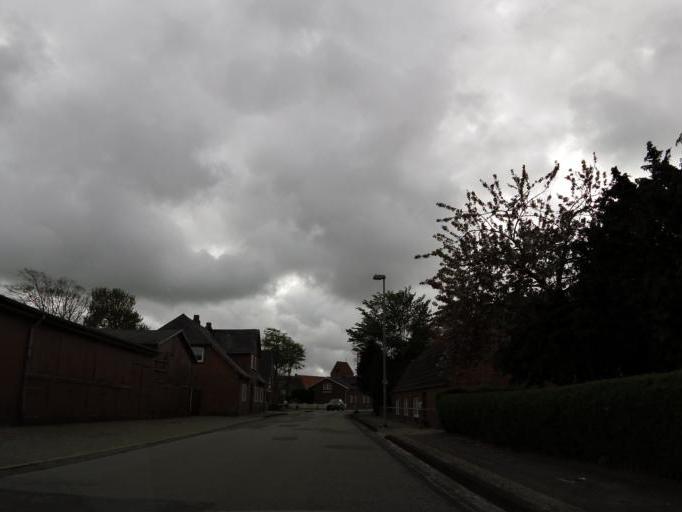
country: DE
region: Schleswig-Holstein
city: Niebull
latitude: 54.7787
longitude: 8.8173
